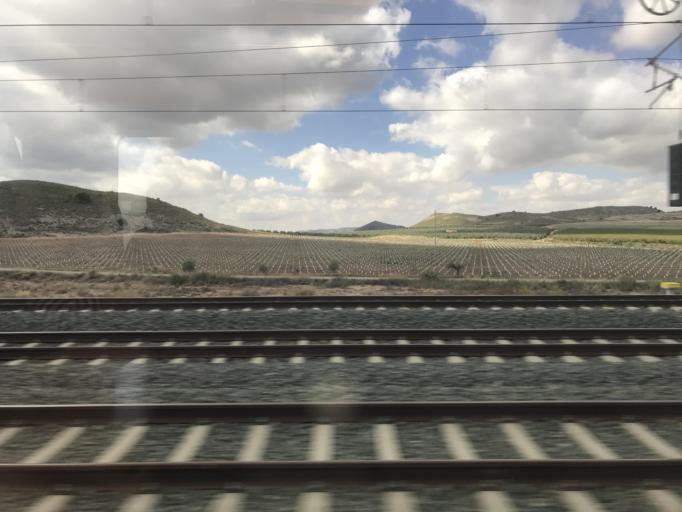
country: ES
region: Valencia
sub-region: Provincia de Alicante
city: Villena
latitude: 38.5881
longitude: -0.8750
